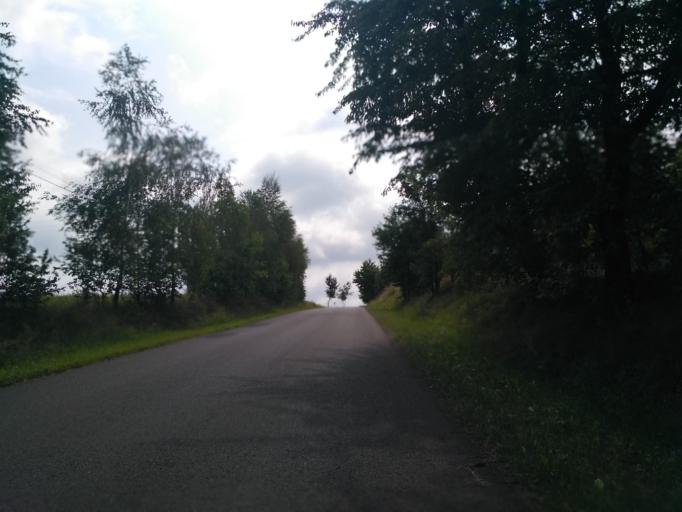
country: PL
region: Subcarpathian Voivodeship
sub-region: Powiat rzeszowski
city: Chmielnik
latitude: 50.0074
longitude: 22.1500
